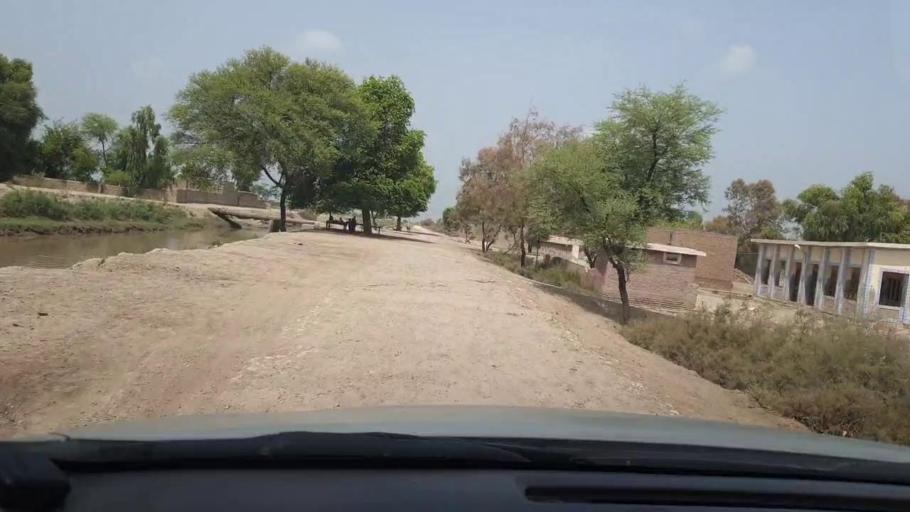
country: PK
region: Sindh
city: Garhi Yasin
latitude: 28.0130
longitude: 68.5344
